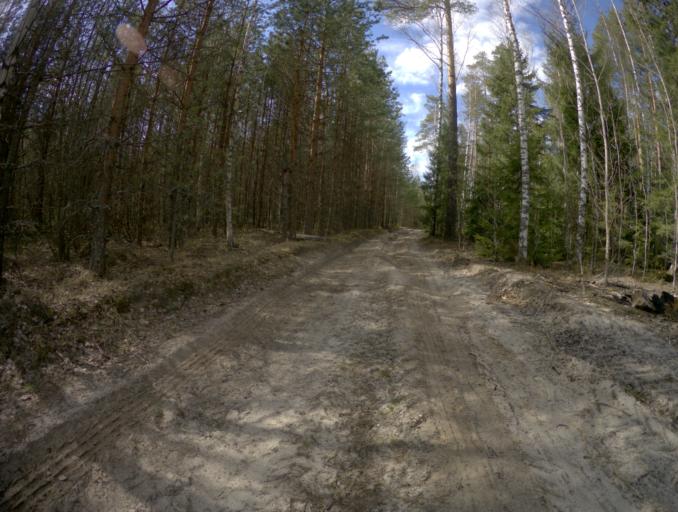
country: RU
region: Vladimir
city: Vorsha
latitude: 55.8769
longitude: 40.1798
